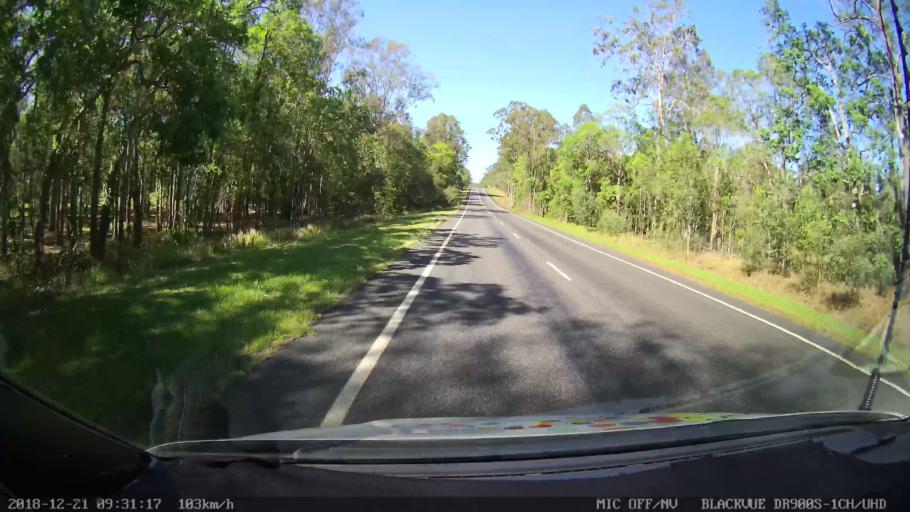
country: AU
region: New South Wales
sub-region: Clarence Valley
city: Maclean
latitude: -29.4583
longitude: 152.9906
